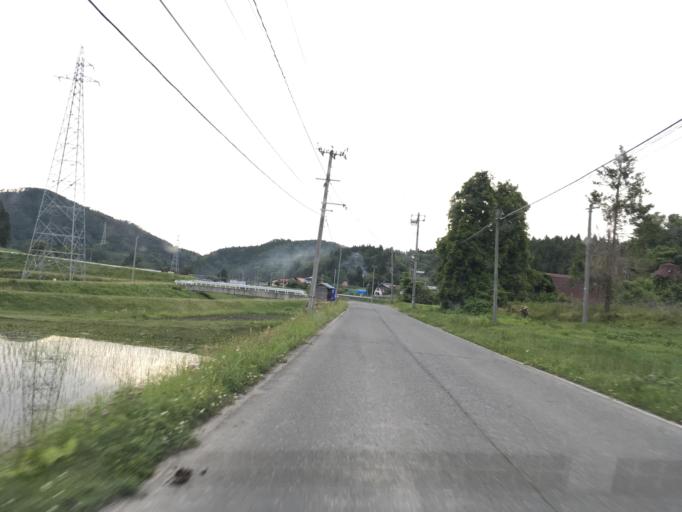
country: JP
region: Iwate
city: Mizusawa
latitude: 39.1714
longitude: 141.2977
